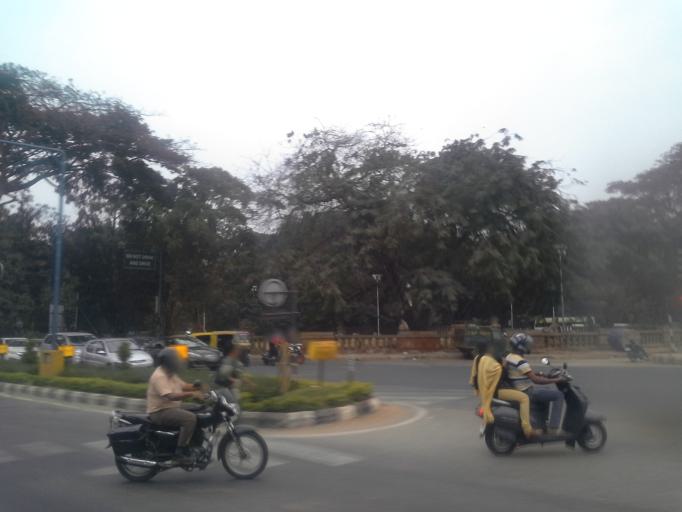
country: IN
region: Karnataka
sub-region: Bangalore Urban
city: Bangalore
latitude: 12.9808
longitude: 77.5974
